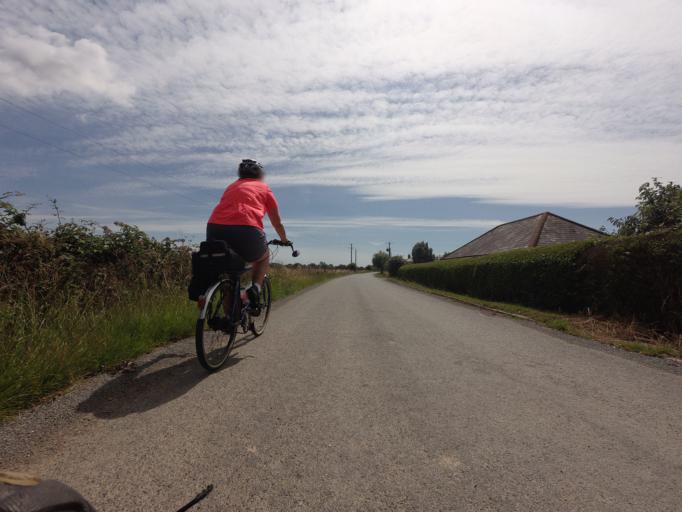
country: GB
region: England
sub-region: Kent
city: Stone
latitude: 51.0061
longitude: 0.7964
